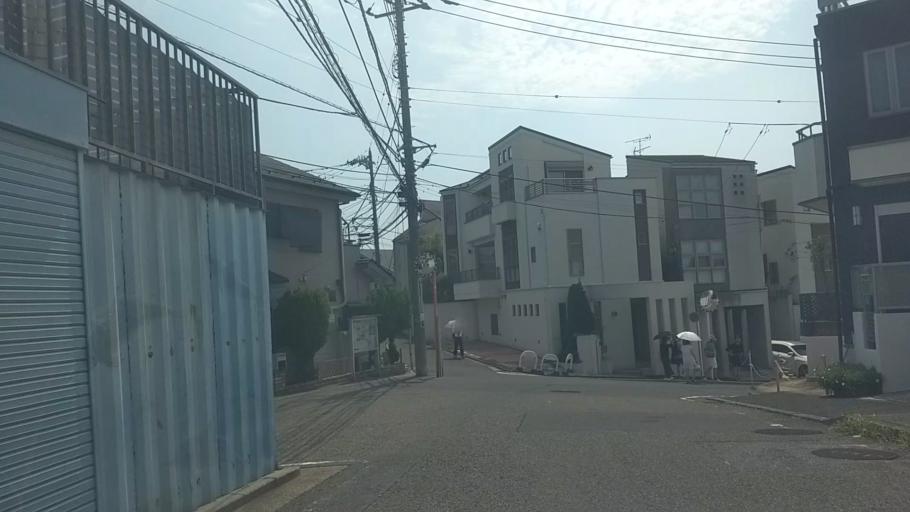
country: JP
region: Kanagawa
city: Yokohama
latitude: 35.4866
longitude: 139.6308
